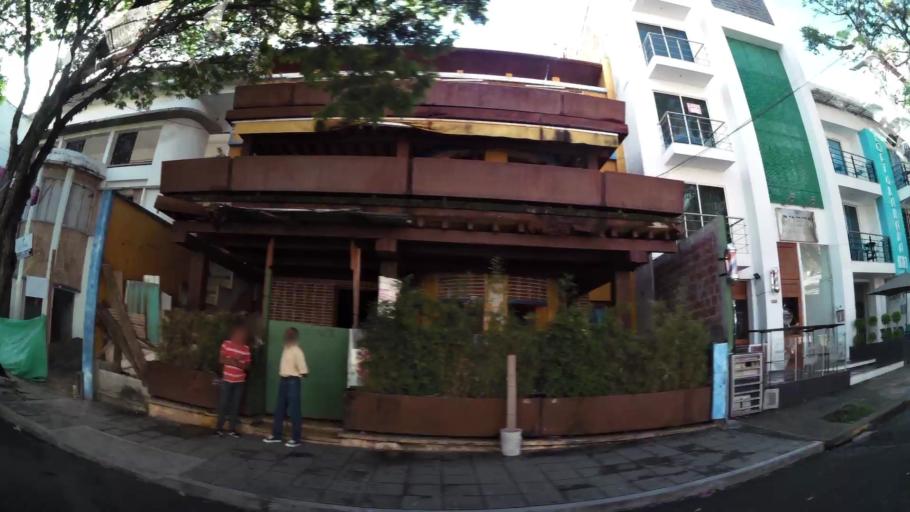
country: CO
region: Valle del Cauca
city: Cali
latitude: 3.4571
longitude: -76.5359
